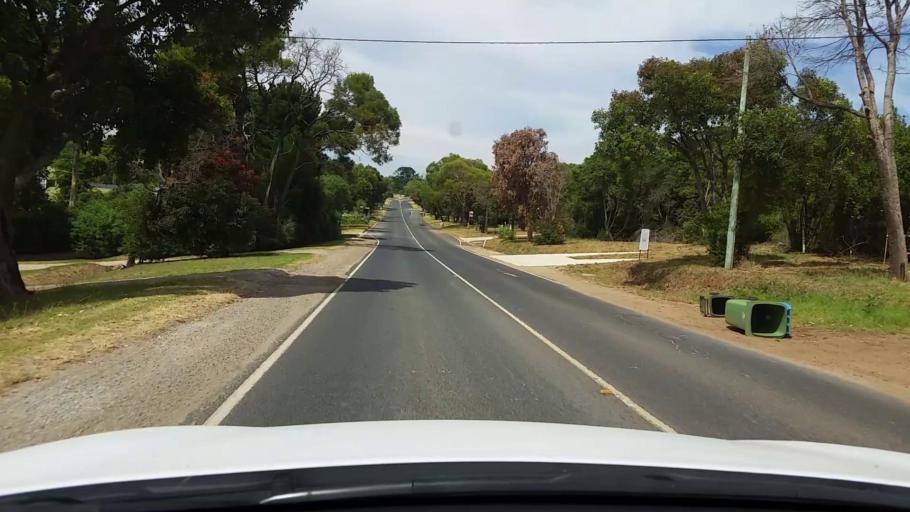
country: AU
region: Victoria
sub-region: Mornington Peninsula
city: Merricks
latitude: -38.4701
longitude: 145.0198
